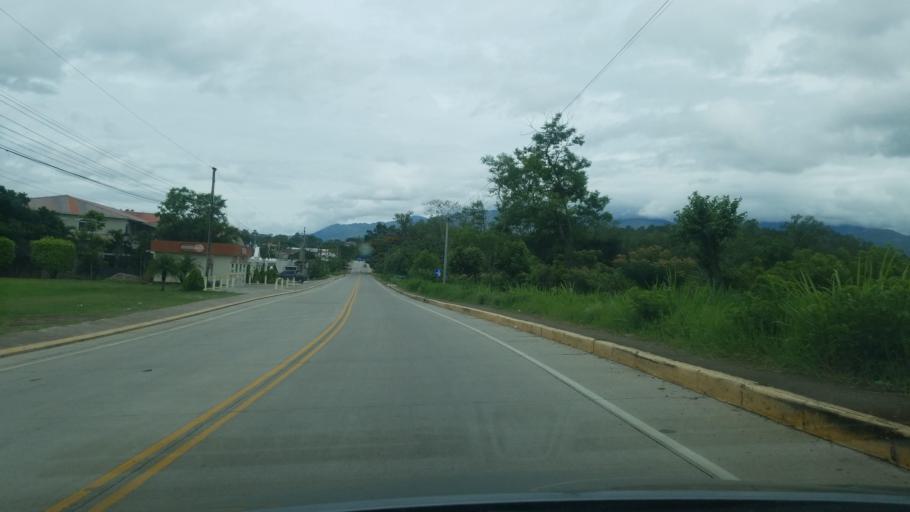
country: HN
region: Copan
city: La Entrada
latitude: 15.0701
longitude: -88.7657
